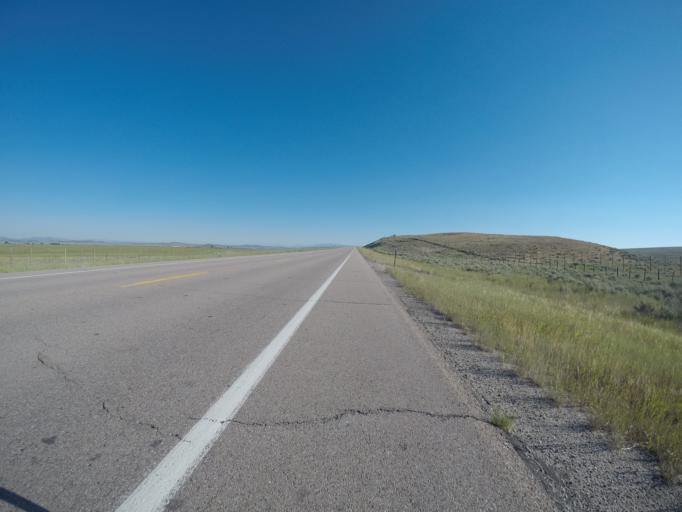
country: US
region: Wyoming
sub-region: Sublette County
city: Pinedale
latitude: 42.9407
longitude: -110.0829
